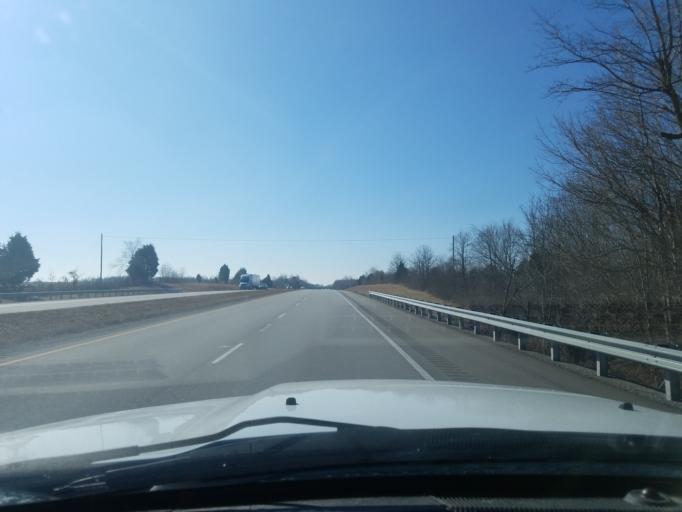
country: US
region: Kentucky
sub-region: Grayson County
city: Leitchfield
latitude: 37.5407
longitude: -86.1307
